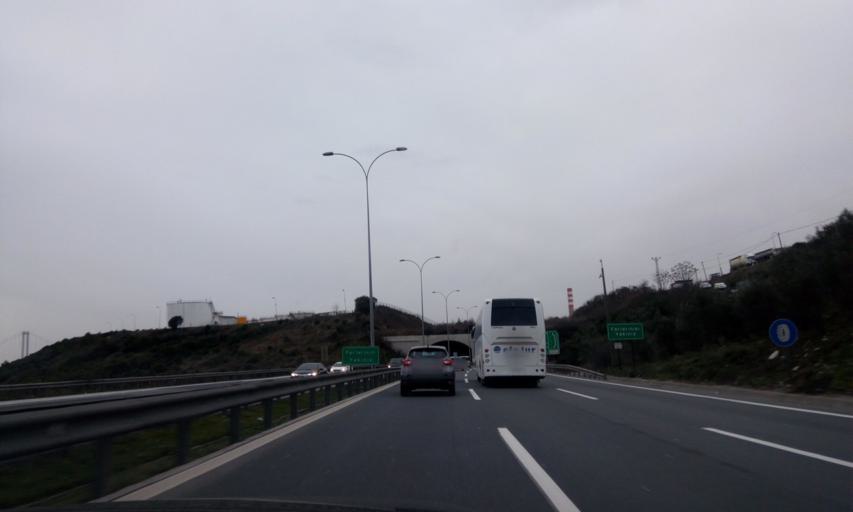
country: TR
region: Kocaeli
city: Tavsancil
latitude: 40.7736
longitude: 29.5530
